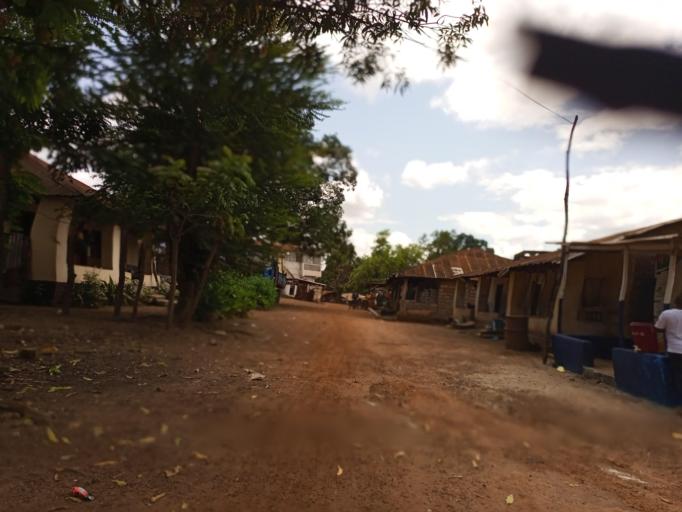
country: SL
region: Northern Province
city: Kamakwie
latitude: 9.4977
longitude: -12.2433
